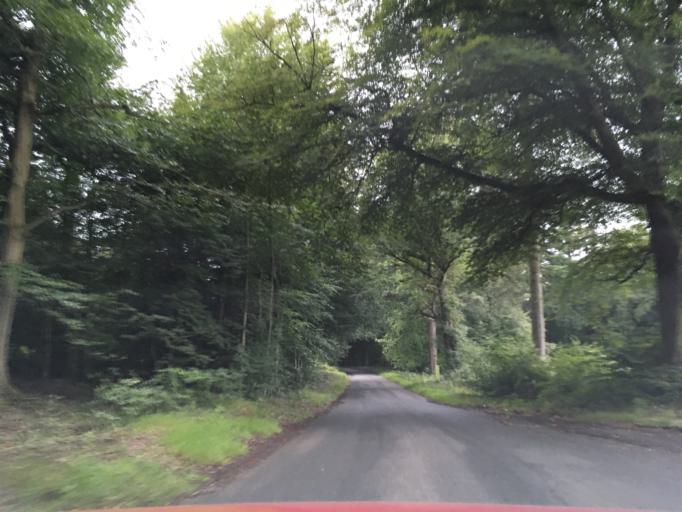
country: GB
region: Wales
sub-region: Newport
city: Llanvaches
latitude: 51.6496
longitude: -2.8372
